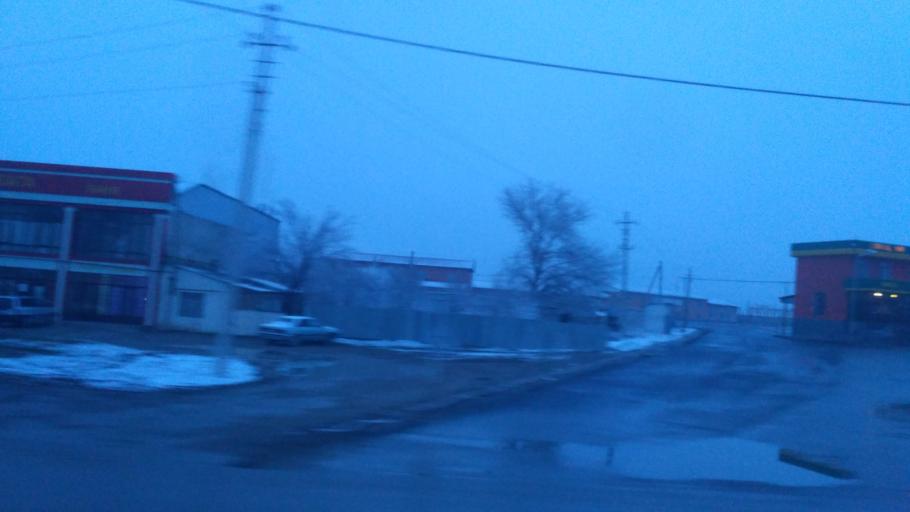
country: KZ
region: Ongtustik Qazaqstan
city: Shymkent
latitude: 42.3635
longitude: 69.5180
